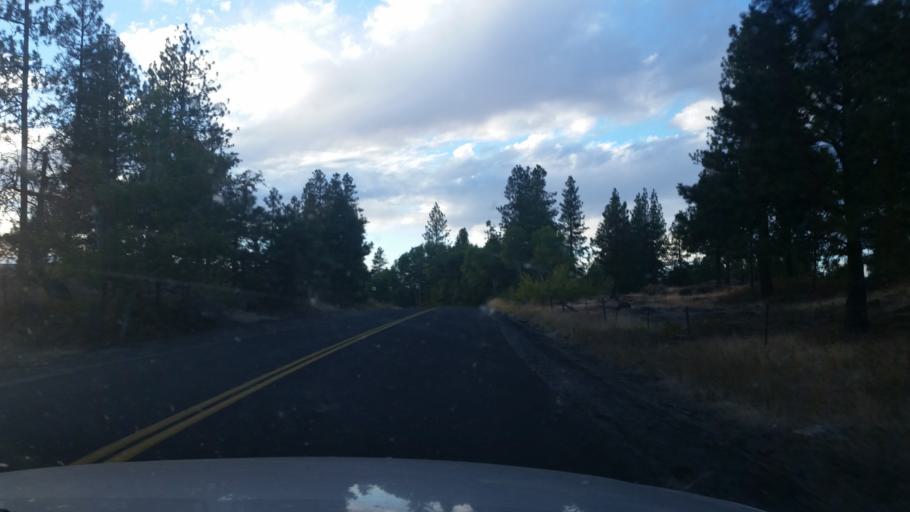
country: US
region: Washington
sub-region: Spokane County
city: Medical Lake
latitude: 47.5441
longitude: -117.6959
